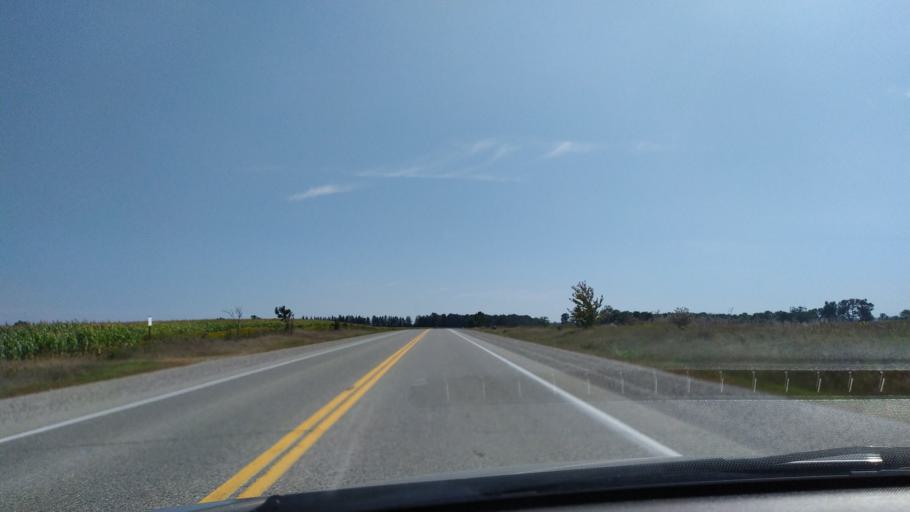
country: CA
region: Ontario
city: Ingersoll
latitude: 43.0919
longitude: -80.8689
